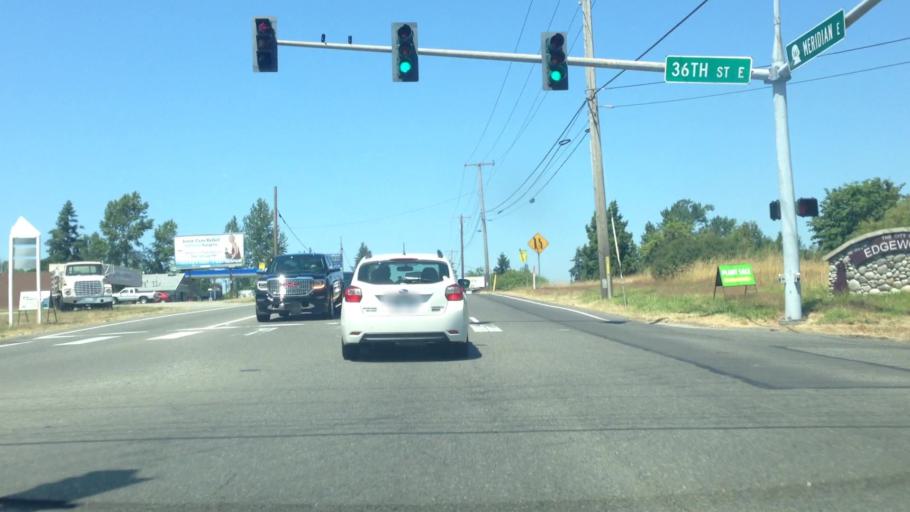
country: US
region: Washington
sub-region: Pierce County
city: North Puyallup
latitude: 47.2248
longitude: -122.2940
